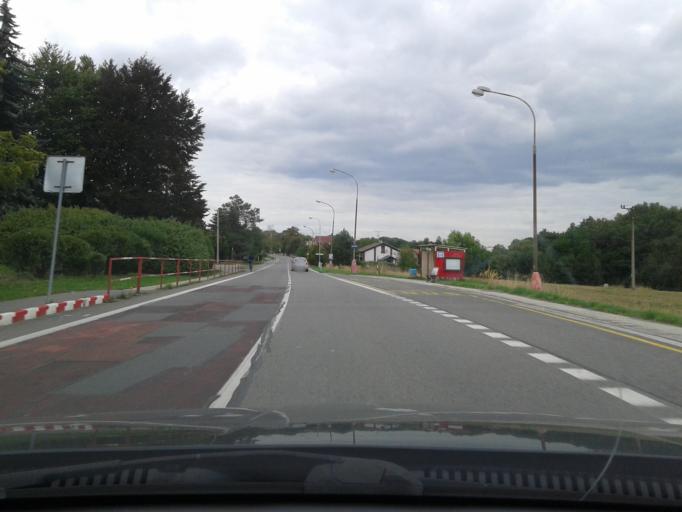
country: CZ
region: Moravskoslezsky
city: Orlova
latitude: 49.8658
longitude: 18.4446
